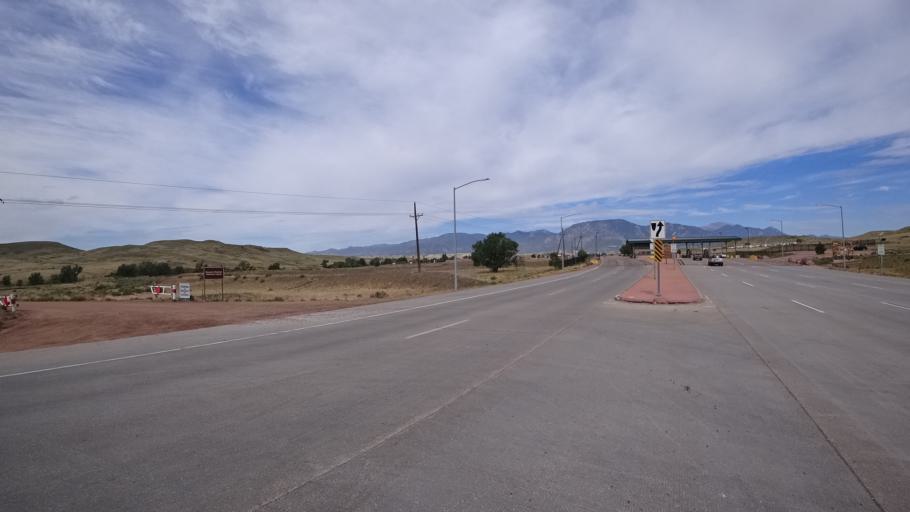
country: US
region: Colorado
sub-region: El Paso County
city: Security-Widefield
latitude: 38.7252
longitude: -104.7384
